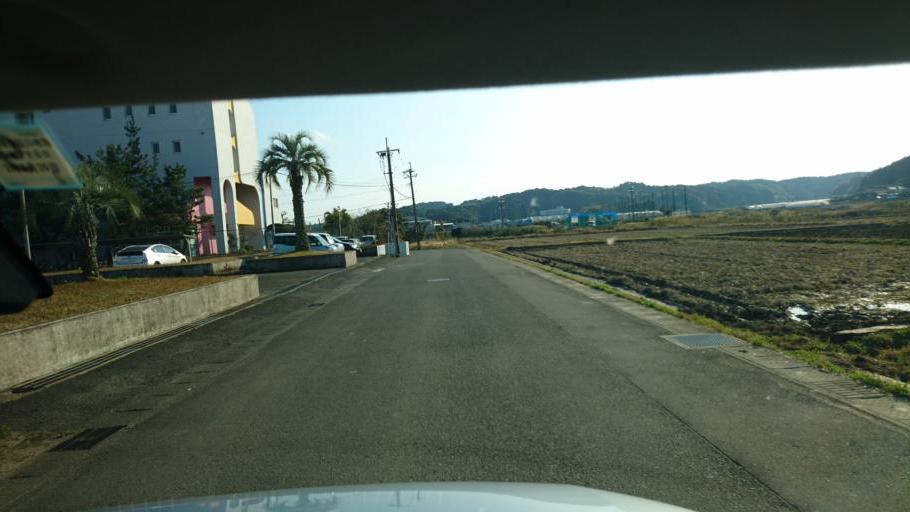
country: JP
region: Miyazaki
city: Miyazaki-shi
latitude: 32.0061
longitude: 131.4396
